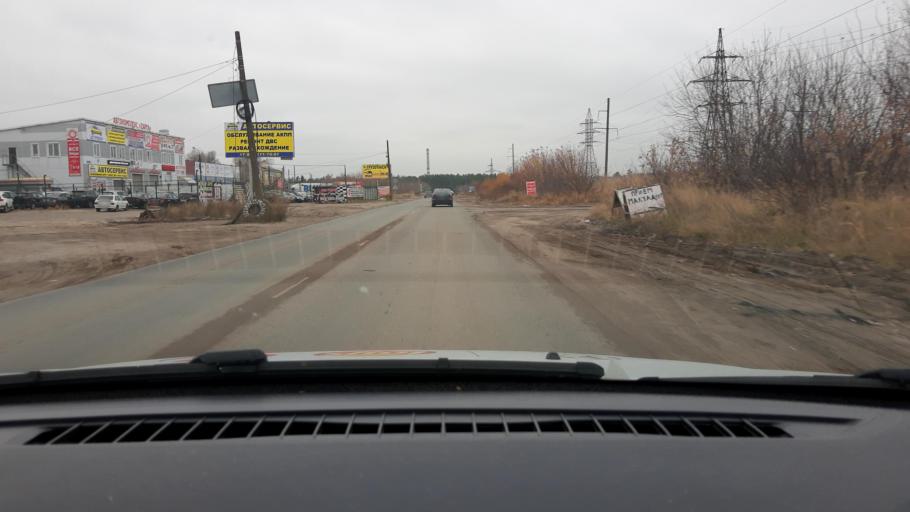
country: RU
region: Nizjnij Novgorod
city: Dzerzhinsk
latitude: 56.2476
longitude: 43.4207
